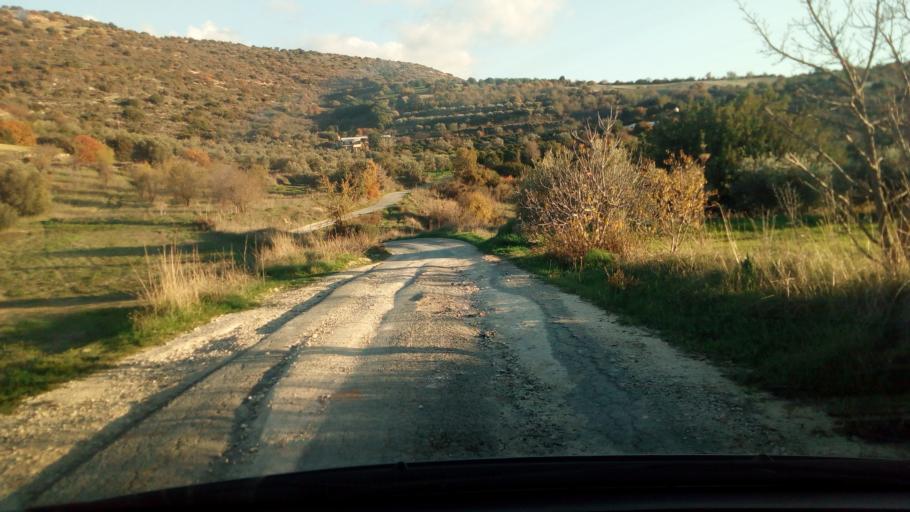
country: CY
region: Pafos
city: Polis
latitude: 34.9847
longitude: 32.4777
